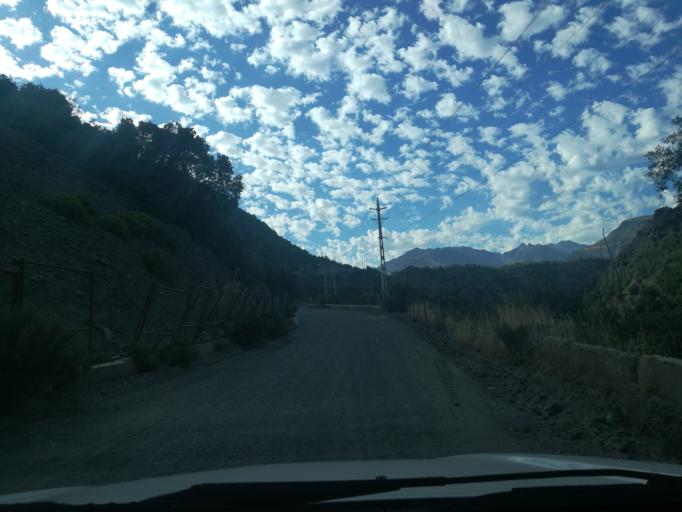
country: CL
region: O'Higgins
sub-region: Provincia de Cachapoal
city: Machali
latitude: -34.2810
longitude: -70.4436
